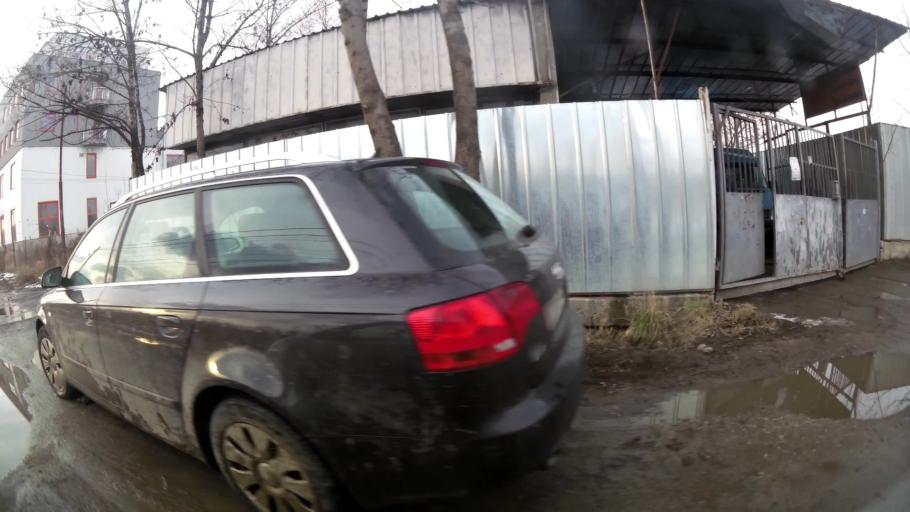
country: BG
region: Sofia-Capital
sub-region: Stolichna Obshtina
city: Sofia
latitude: 42.7313
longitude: 23.3424
